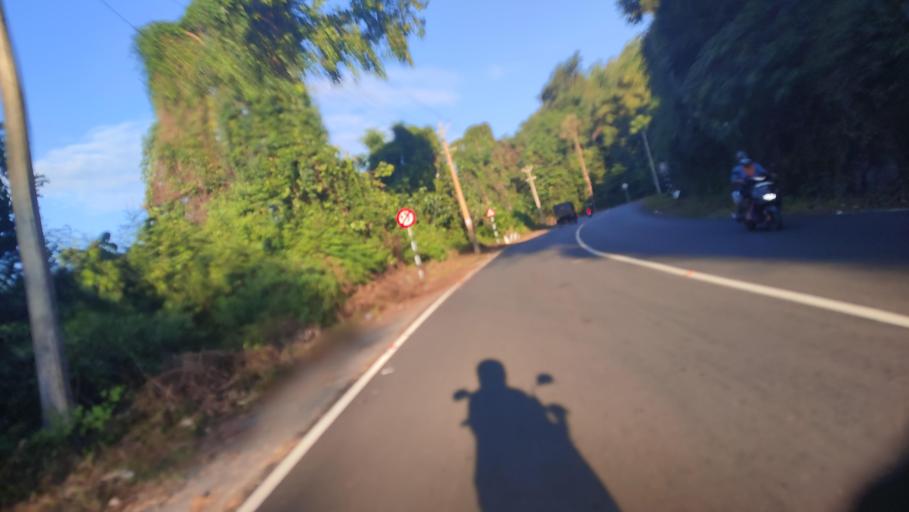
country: IN
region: Kerala
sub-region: Kasaragod District
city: Kasaragod
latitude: 12.4596
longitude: 75.0884
